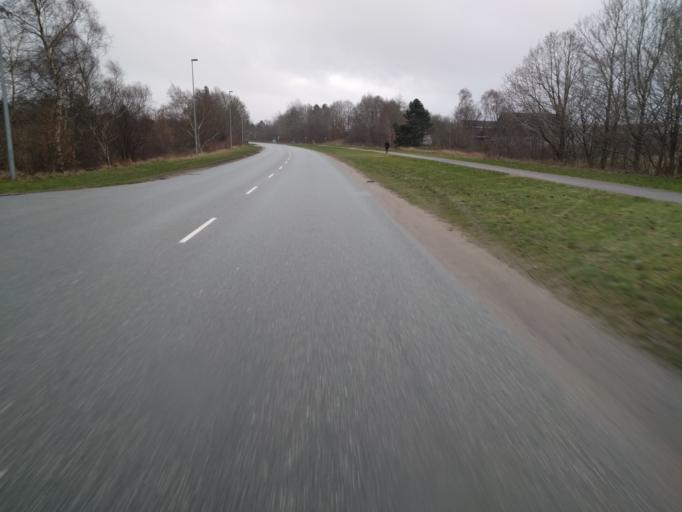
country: DK
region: Central Jutland
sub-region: Viborg Kommune
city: Viborg
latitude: 56.4594
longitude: 9.4449
